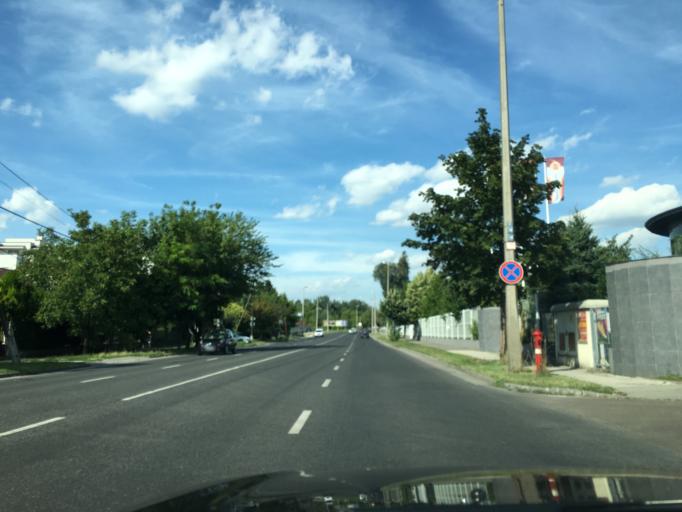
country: HU
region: Budapest
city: Budapest IV. keruelet
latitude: 47.5869
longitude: 19.0957
